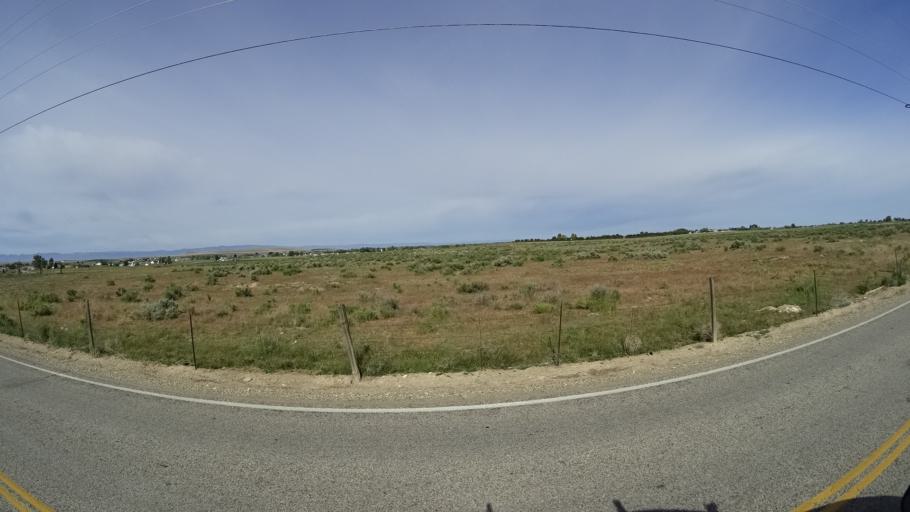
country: US
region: Idaho
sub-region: Ada County
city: Kuna
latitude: 43.4795
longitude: -116.3345
